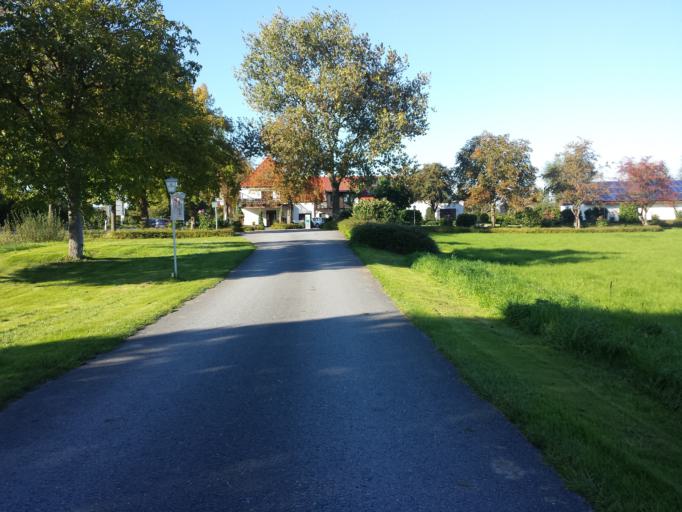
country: DE
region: North Rhine-Westphalia
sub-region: Regierungsbezirk Detmold
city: Langenberg
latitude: 51.7679
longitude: 8.3251
